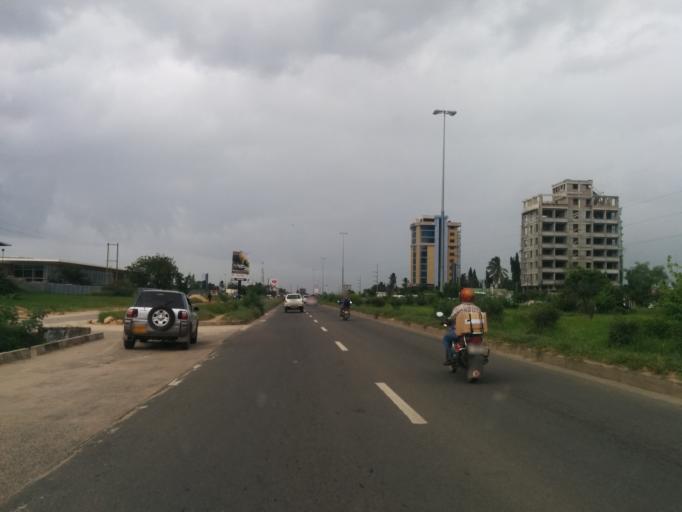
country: TZ
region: Dar es Salaam
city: Magomeni
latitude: -6.7763
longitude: 39.2191
